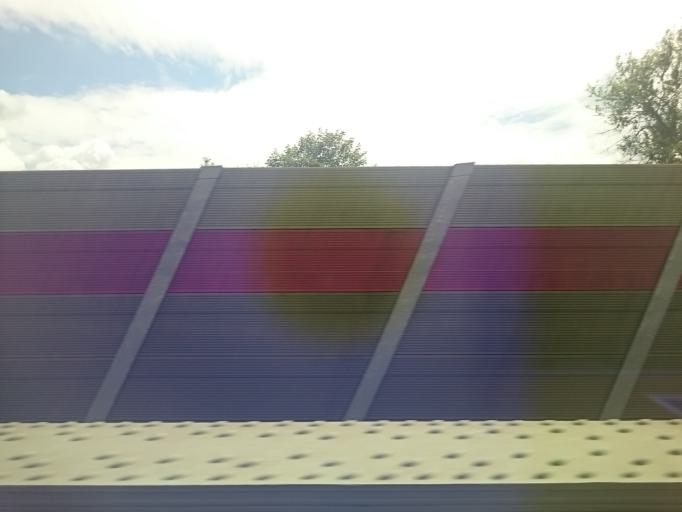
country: AT
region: Tyrol
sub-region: Politischer Bezirk Kufstein
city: Angath
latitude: 47.4954
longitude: 12.0682
